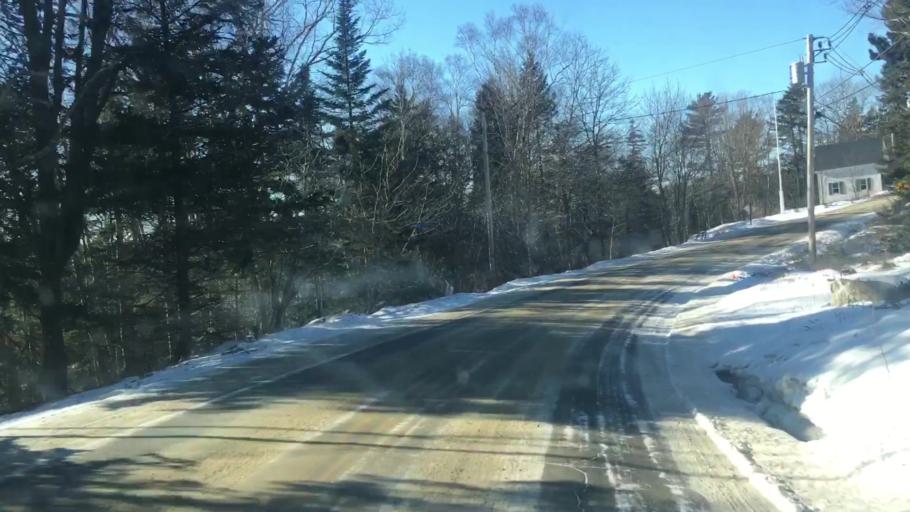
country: US
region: Maine
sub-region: Hancock County
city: Castine
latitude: 44.3400
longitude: -68.7333
